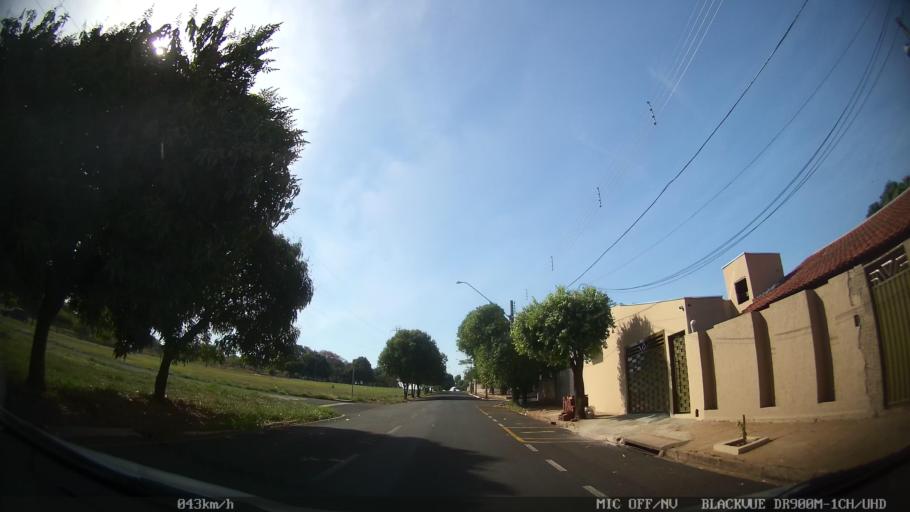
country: BR
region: Sao Paulo
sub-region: Sao Jose Do Rio Preto
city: Sao Jose do Rio Preto
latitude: -20.7966
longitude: -49.4167
